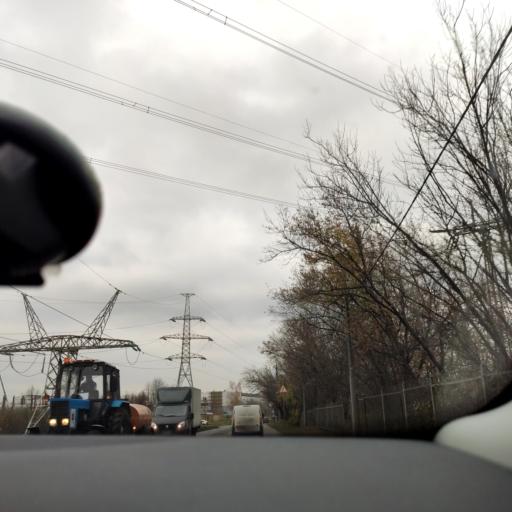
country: RU
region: Moscow
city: Kapotnya
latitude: 55.6659
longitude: 37.8082
